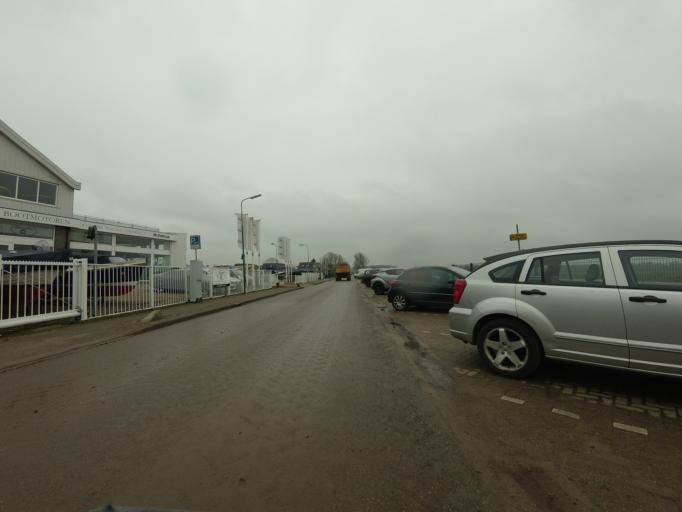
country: NL
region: Utrecht
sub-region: Stichtse Vecht
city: Breukelen
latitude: 52.1833
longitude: 5.0189
